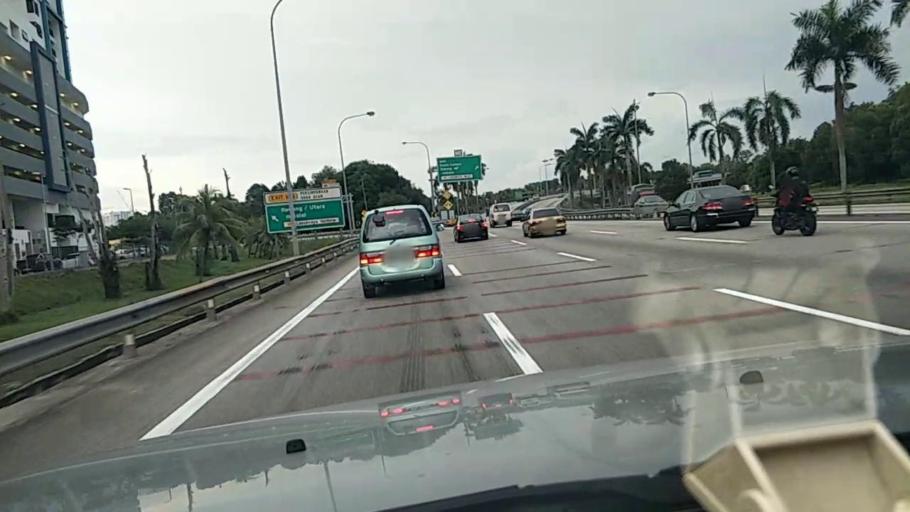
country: MY
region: Selangor
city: Shah Alam
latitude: 3.0897
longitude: 101.5493
